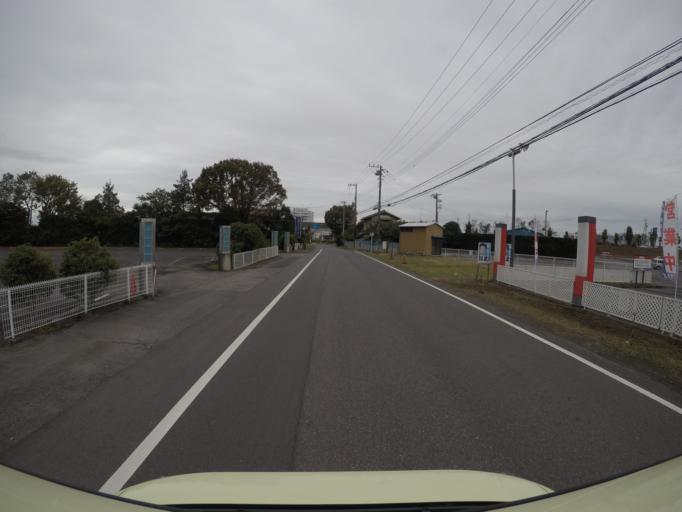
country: JP
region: Ibaraki
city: Naka
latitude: 36.0888
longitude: 140.1821
